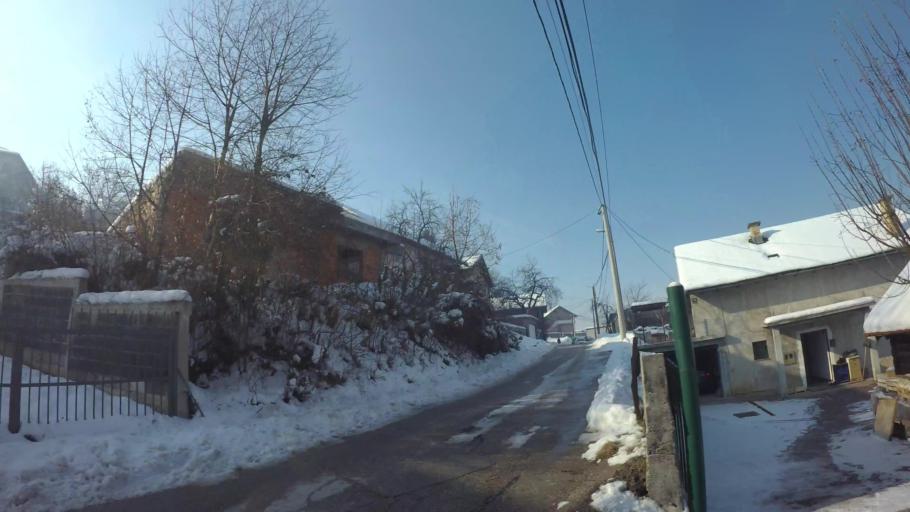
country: BA
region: Federation of Bosnia and Herzegovina
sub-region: Kanton Sarajevo
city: Sarajevo
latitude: 43.8432
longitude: 18.3872
